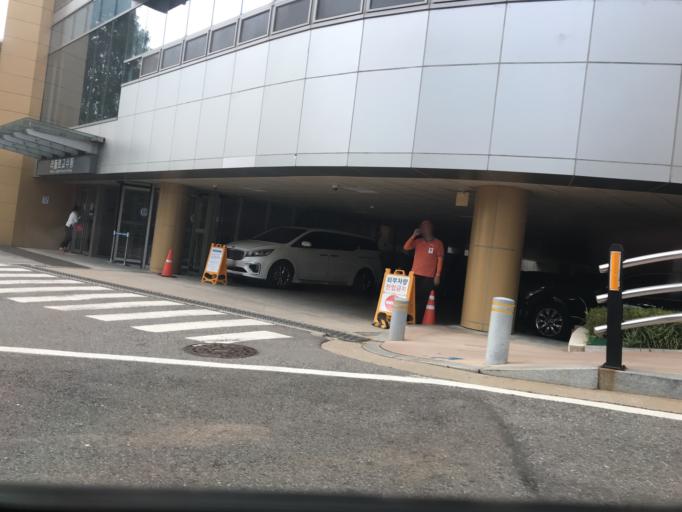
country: KR
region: Seoul
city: Seoul
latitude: 37.5634
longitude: 126.9414
